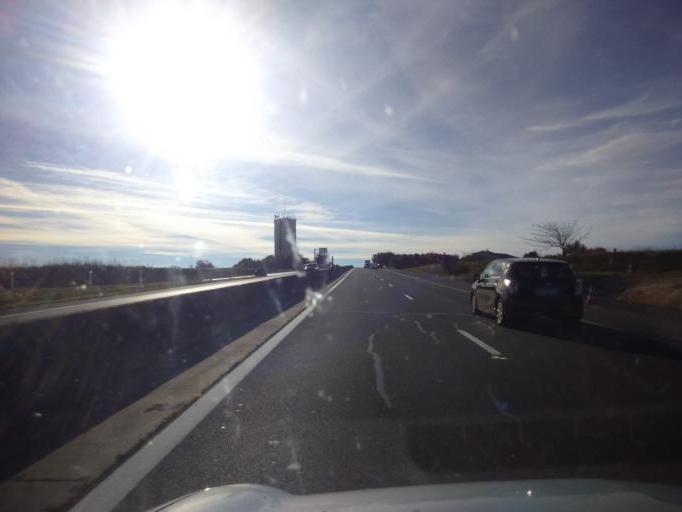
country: FR
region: Poitou-Charentes
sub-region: Departement de la Charente-Maritime
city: Aytre
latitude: 46.1414
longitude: -1.1063
